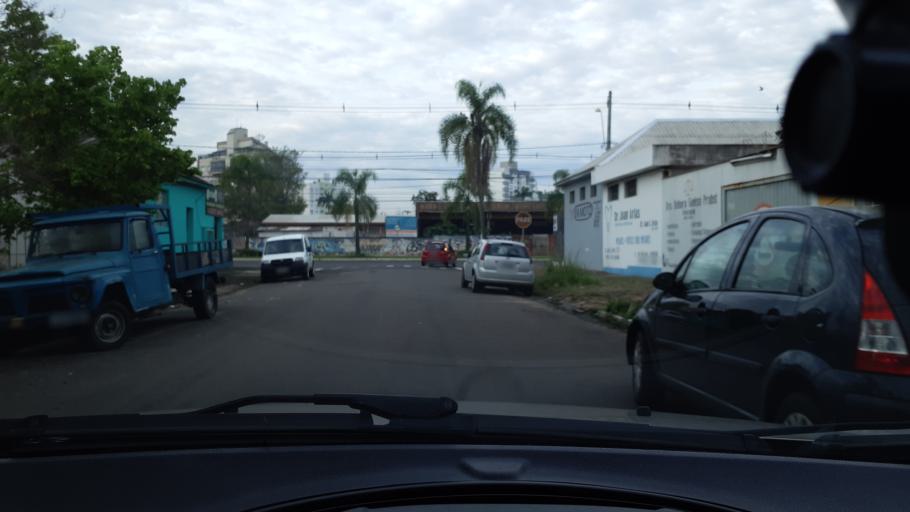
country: BR
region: Rio Grande do Sul
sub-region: Sao Leopoldo
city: Sao Leopoldo
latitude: -29.7713
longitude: -51.1508
